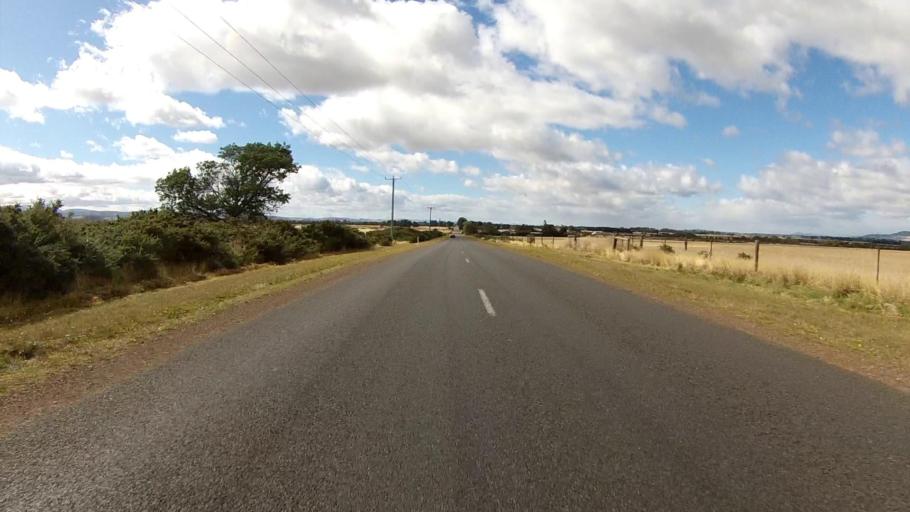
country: AU
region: Tasmania
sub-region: Northern Midlands
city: Evandale
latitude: -41.5945
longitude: 147.2691
